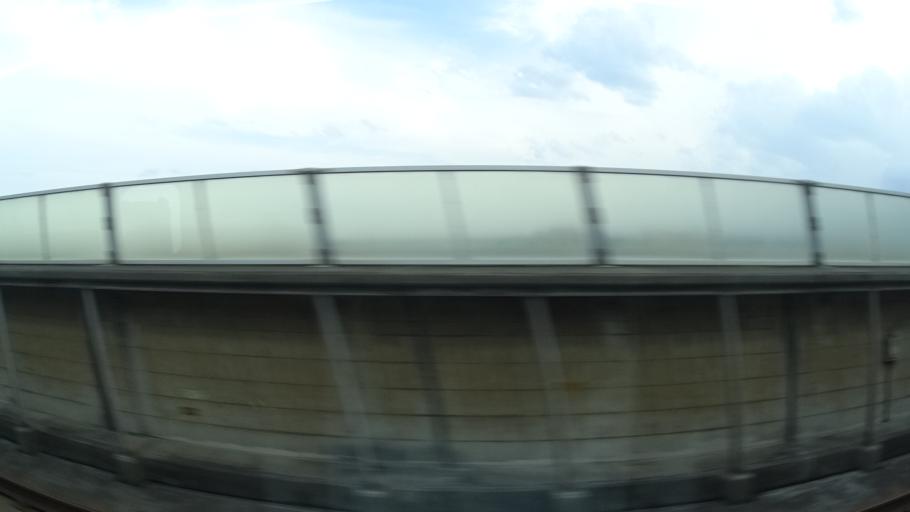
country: JP
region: Saitama
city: Kumagaya
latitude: 36.1516
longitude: 139.3537
